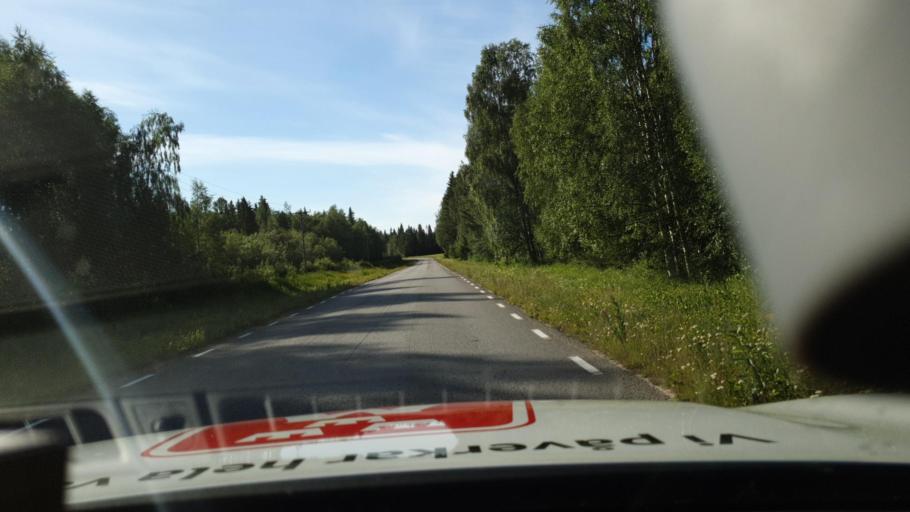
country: SE
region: Norrbotten
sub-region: Kalix Kommun
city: Toere
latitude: 65.8934
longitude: 22.6363
